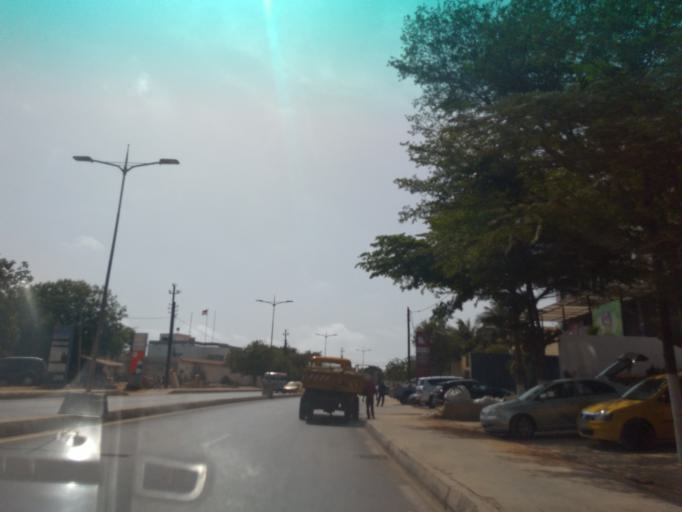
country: SN
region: Dakar
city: Mermoz Boabab
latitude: 14.7040
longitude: -17.4767
